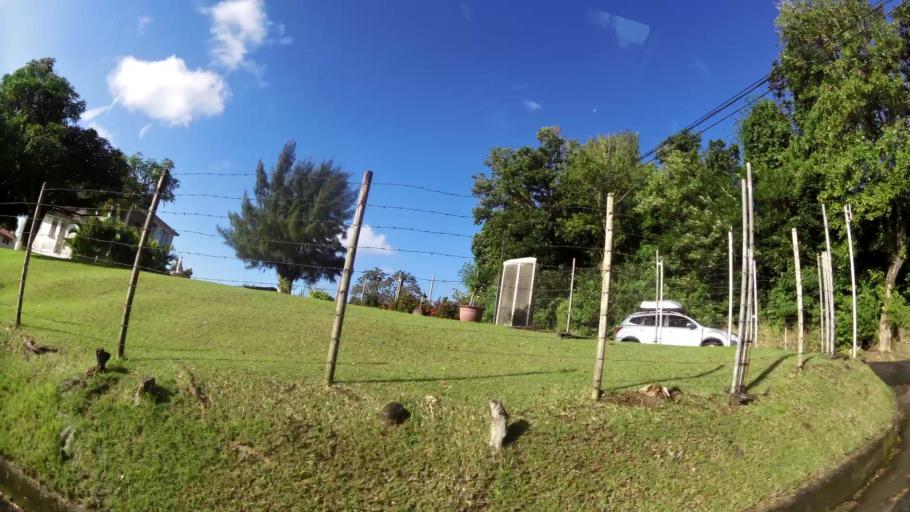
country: MQ
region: Martinique
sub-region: Martinique
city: Le Lamentin
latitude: 14.6303
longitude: -61.0289
